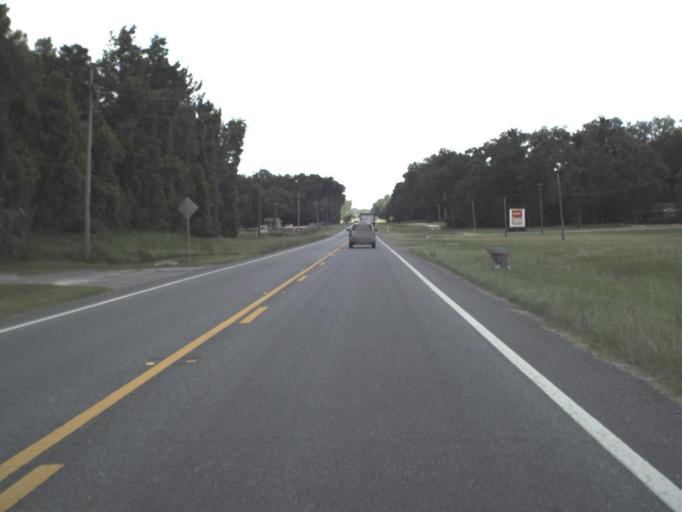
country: US
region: Florida
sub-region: Columbia County
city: Lake City
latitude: 30.1328
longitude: -82.6278
